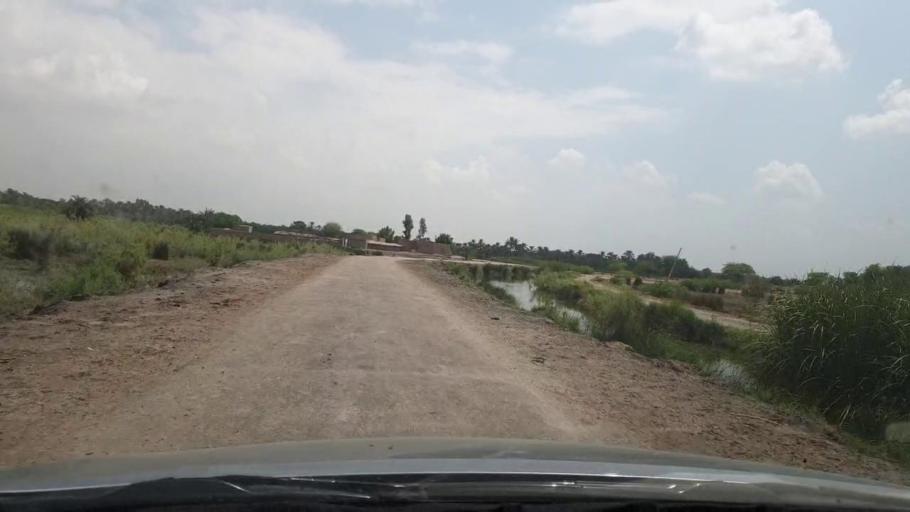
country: PK
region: Sindh
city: Kot Diji
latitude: 27.4021
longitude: 68.7386
